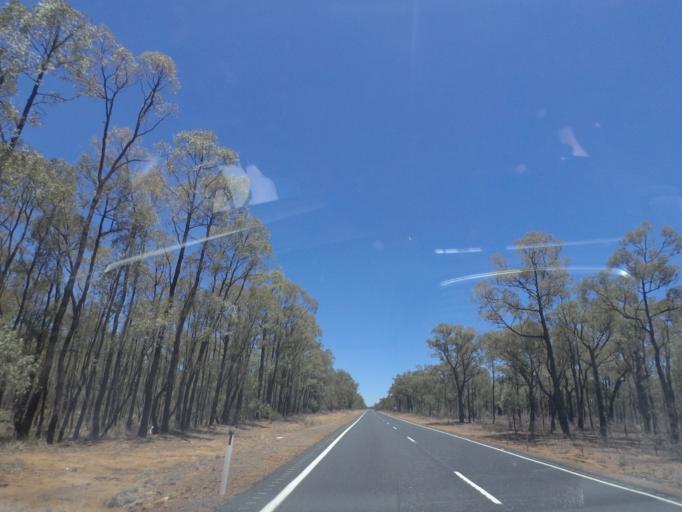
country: AU
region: New South Wales
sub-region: Warrumbungle Shire
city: Coonabarabran
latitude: -30.8609
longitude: 149.4541
